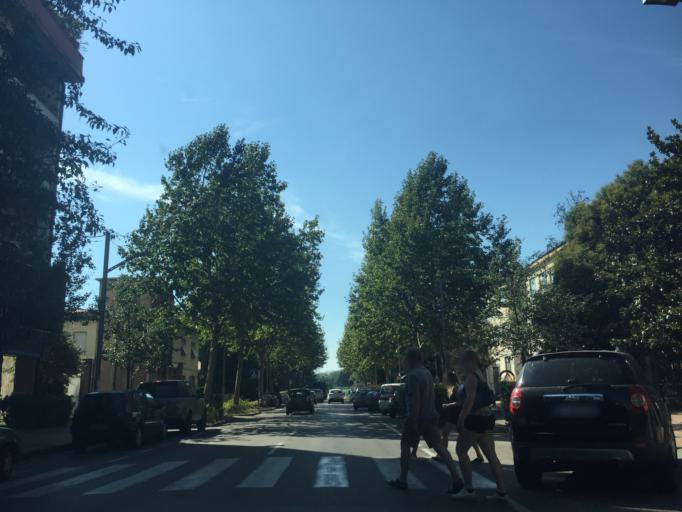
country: IT
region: Tuscany
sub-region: Provincia di Lucca
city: Lucca
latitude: 43.8491
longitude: 10.5052
